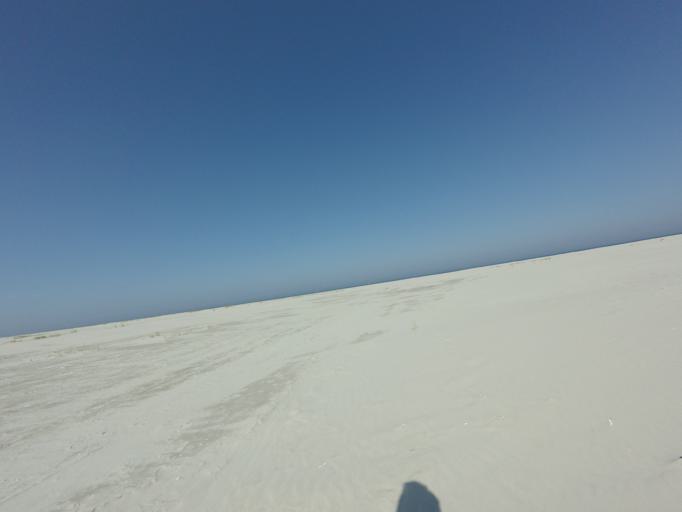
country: NL
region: Friesland
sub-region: Gemeente Schiermonnikoog
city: Schiermonnikoog
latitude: 53.5041
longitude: 6.2447
